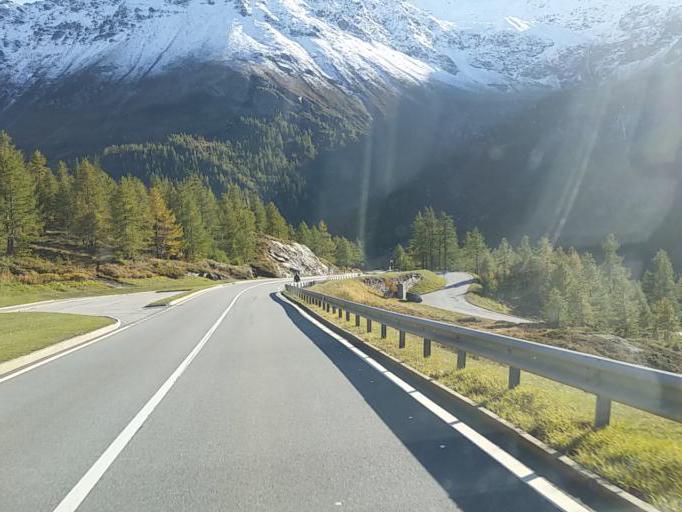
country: CH
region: Valais
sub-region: Brig District
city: Brig
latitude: 46.2317
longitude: 8.0142
